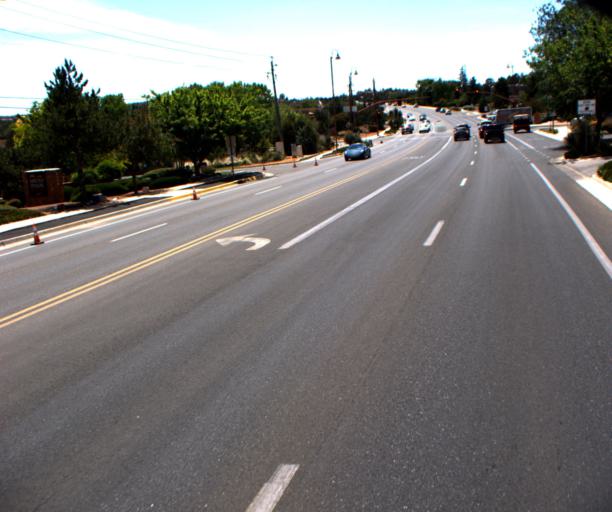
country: US
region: Arizona
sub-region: Yavapai County
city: West Sedona
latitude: 34.8616
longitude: -111.8147
